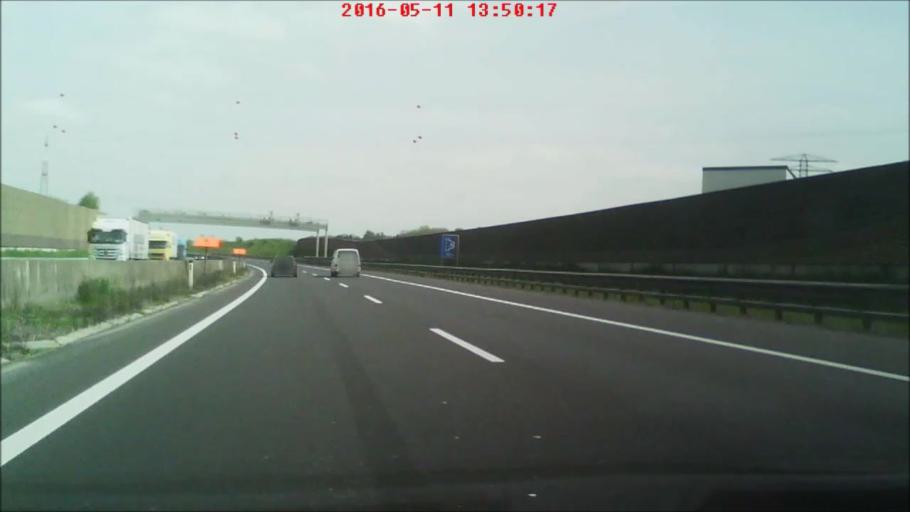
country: AT
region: Upper Austria
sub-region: Politischer Bezirk Vocklabruck
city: Wolfsegg am Hausruck
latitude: 48.1797
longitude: 13.6959
